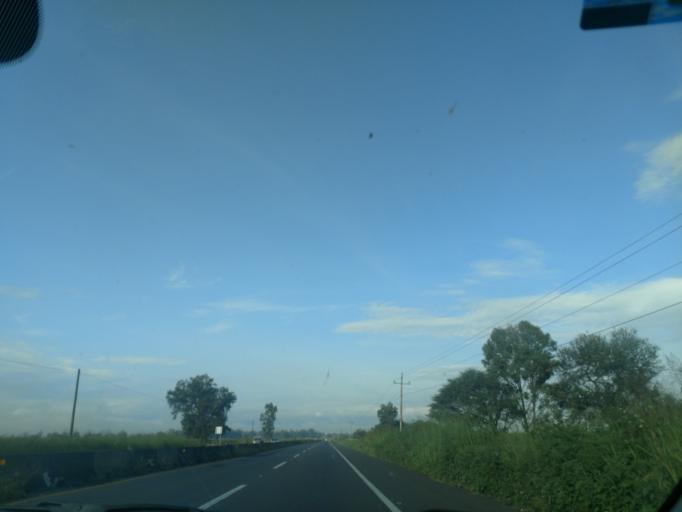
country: MX
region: Jalisco
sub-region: Ameca
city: Los Pocitos
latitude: 20.5434
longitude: -103.9148
